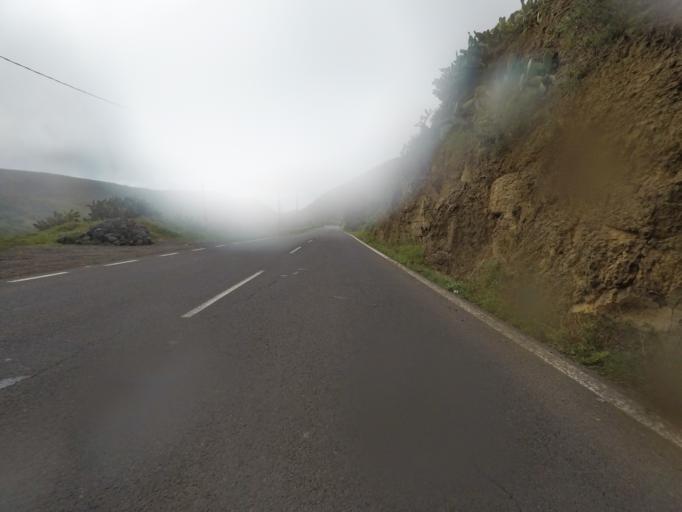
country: ES
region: Canary Islands
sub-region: Provincia de Santa Cruz de Tenerife
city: Vallehermosa
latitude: 28.1389
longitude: -17.3141
